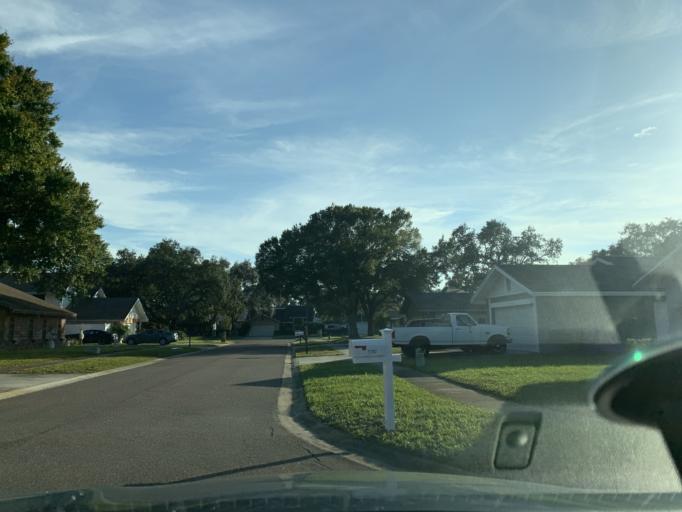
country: US
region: Florida
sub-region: Pinellas County
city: Ridgecrest
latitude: 27.8835
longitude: -82.7989
